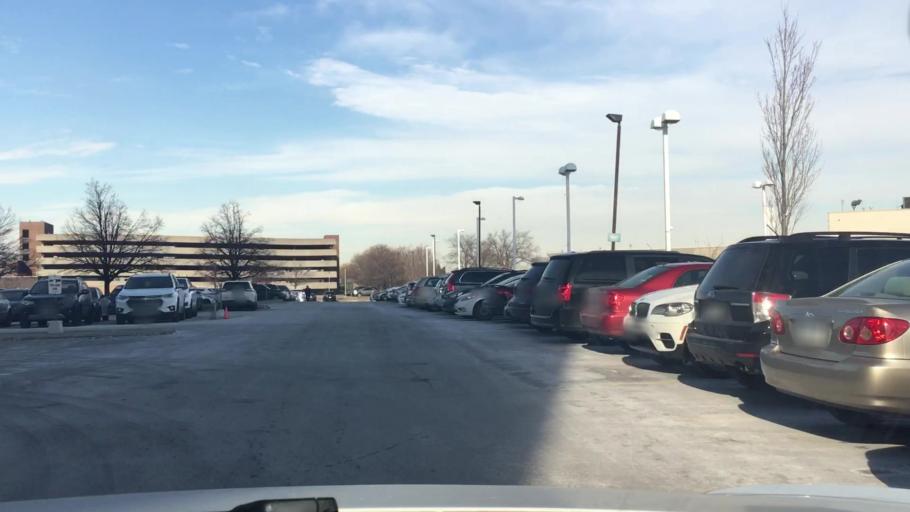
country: CA
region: Ontario
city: Willowdale
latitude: 43.8151
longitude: -79.3466
